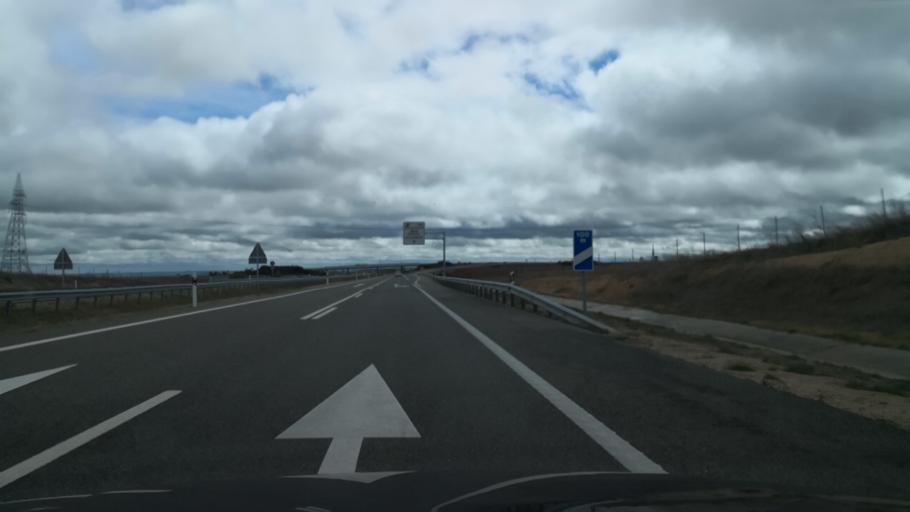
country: ES
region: Castille and Leon
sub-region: Provincia de Zamora
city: Roales
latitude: 41.5826
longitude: -5.7767
